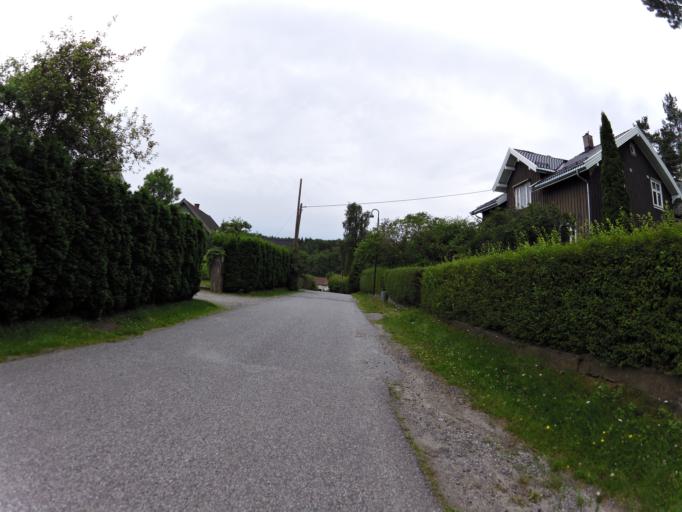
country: NO
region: Akershus
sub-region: Vestby
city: Vestby
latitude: 59.5404
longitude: 10.7436
